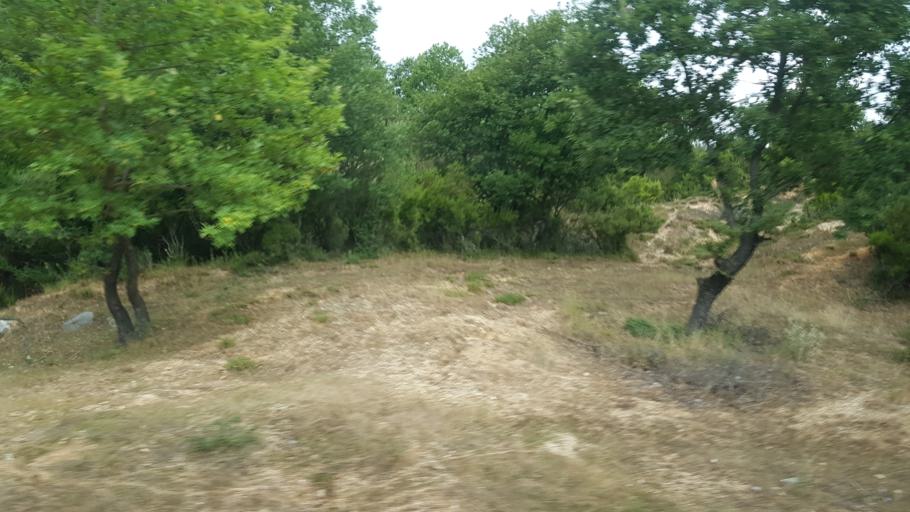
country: AL
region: Vlore
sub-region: Rrethi i Sarandes
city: Dhiver
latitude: 39.9121
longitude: 20.1876
